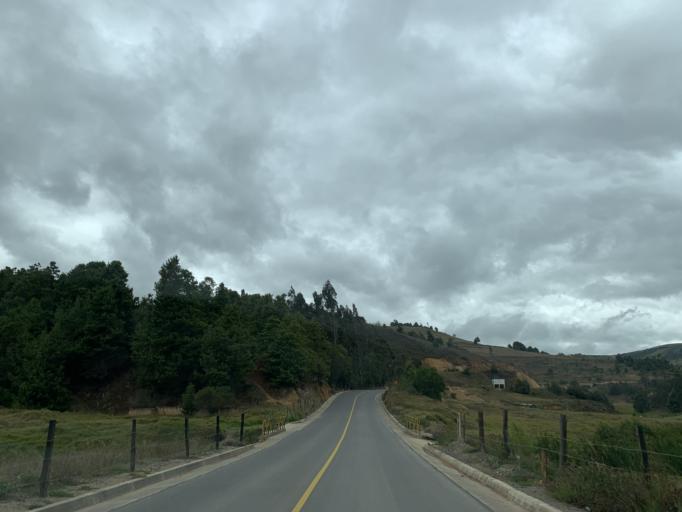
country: CO
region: Boyaca
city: Tunja
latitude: 5.5302
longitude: -73.3278
